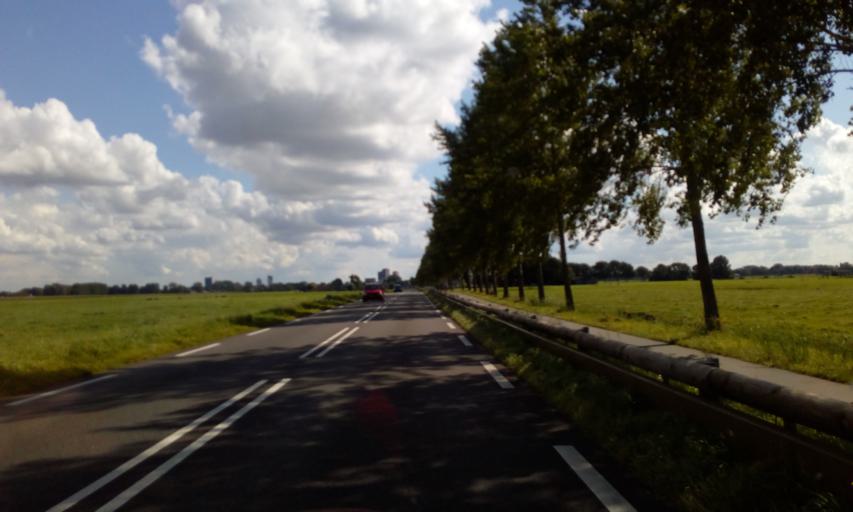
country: NL
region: South Holland
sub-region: Gemeente Zoetermeer
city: Zoetermeer
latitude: 52.0865
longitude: 4.4740
